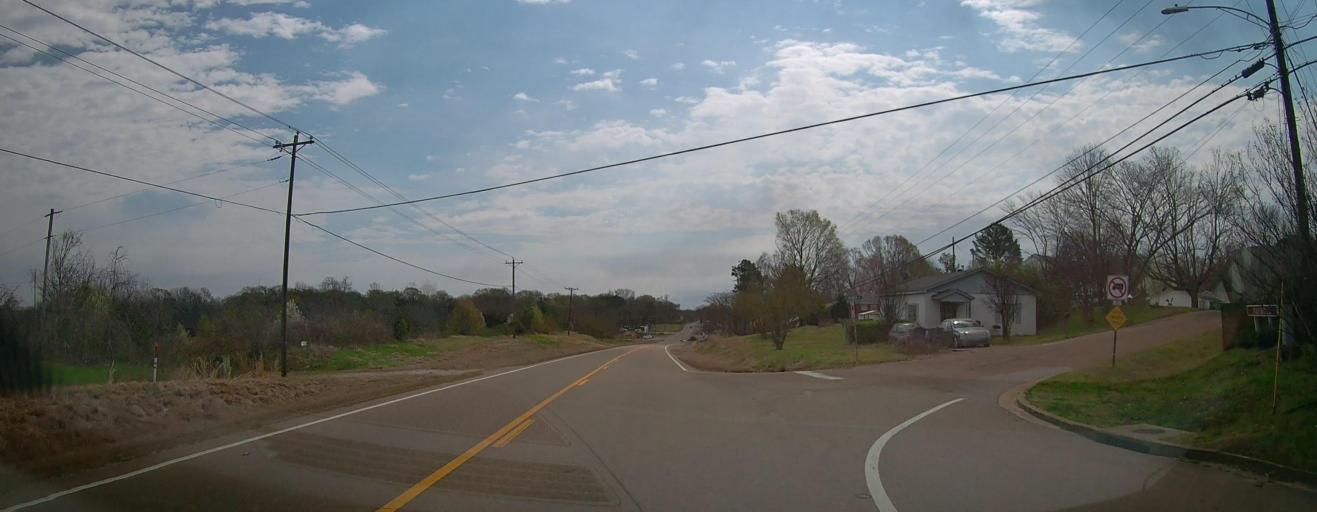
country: US
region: Mississippi
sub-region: De Soto County
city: Olive Branch
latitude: 34.9770
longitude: -89.8485
